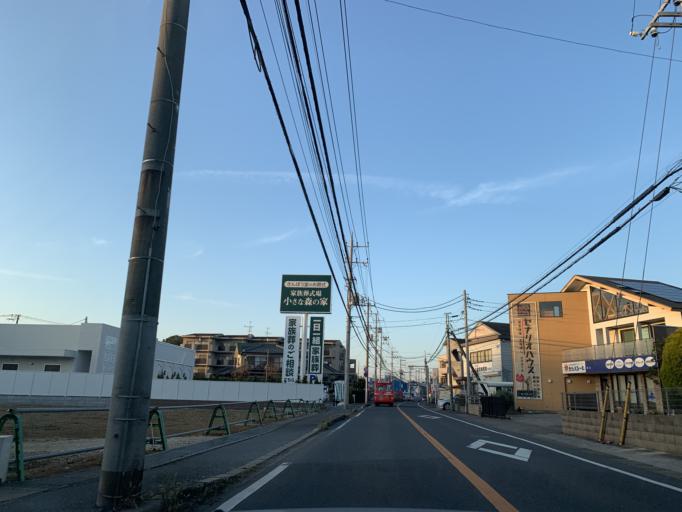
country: JP
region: Chiba
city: Kashiwa
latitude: 35.8776
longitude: 139.9374
